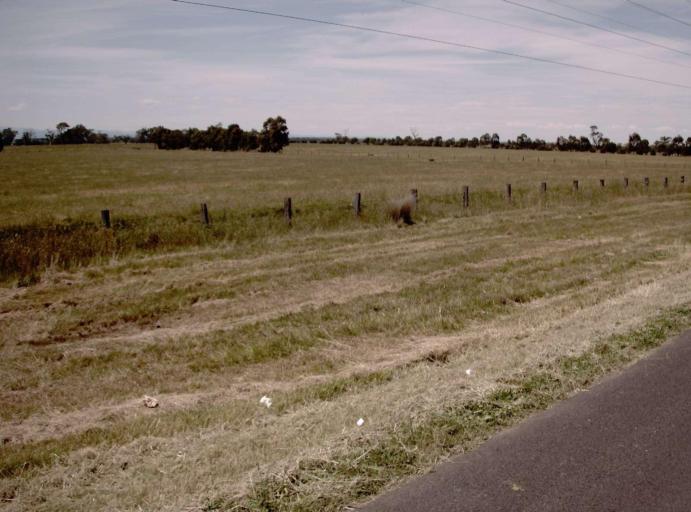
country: AU
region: Victoria
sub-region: Latrobe
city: Traralgon
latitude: -38.1823
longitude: 146.6107
